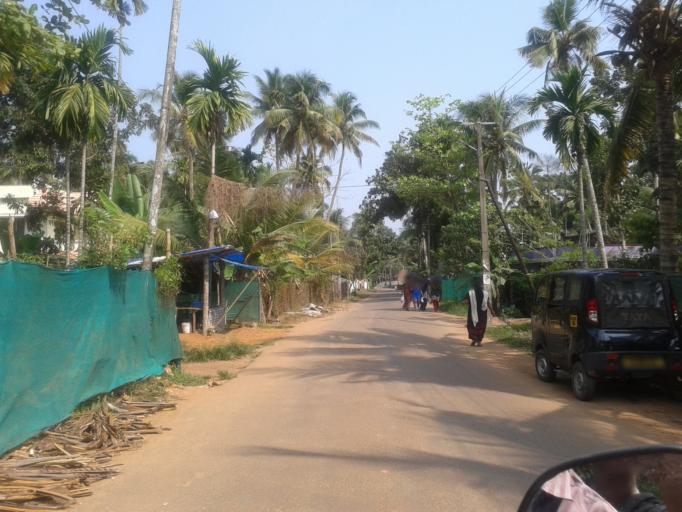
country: IN
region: Kerala
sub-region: Kottayam
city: Changanacheri
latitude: 9.4595
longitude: 76.4433
